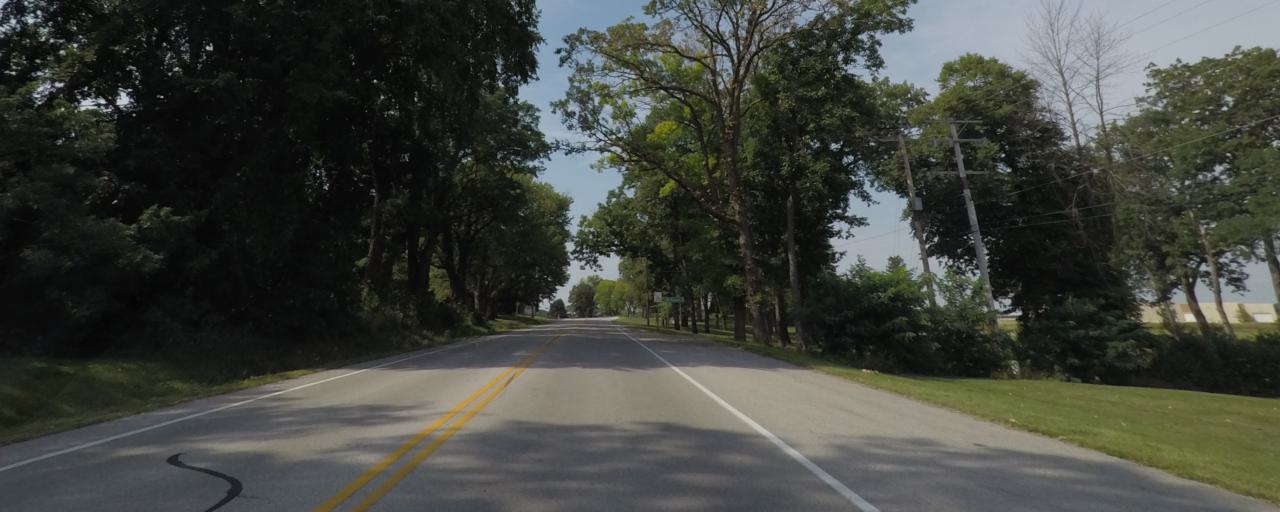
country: US
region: Wisconsin
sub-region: Jefferson County
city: Jefferson
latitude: 42.9921
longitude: -88.8257
